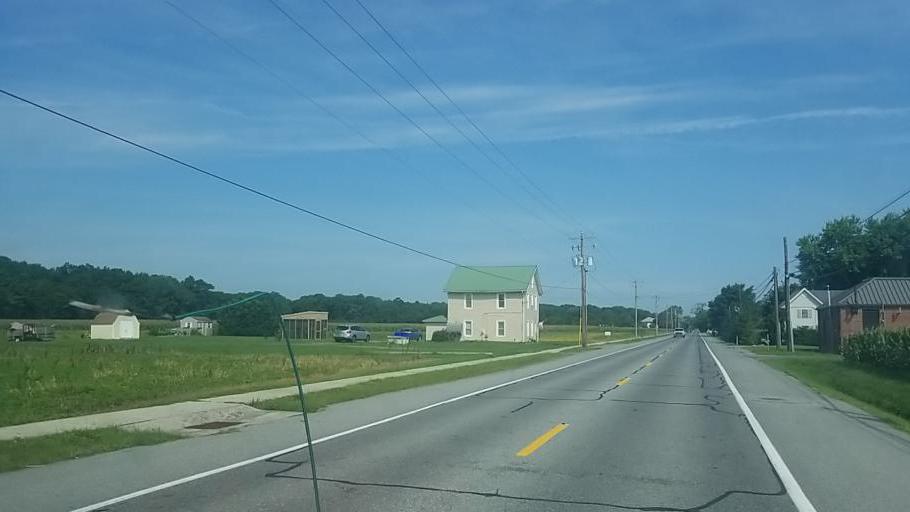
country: US
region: Delaware
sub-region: Sussex County
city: Millsboro
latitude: 38.5407
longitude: -75.2387
